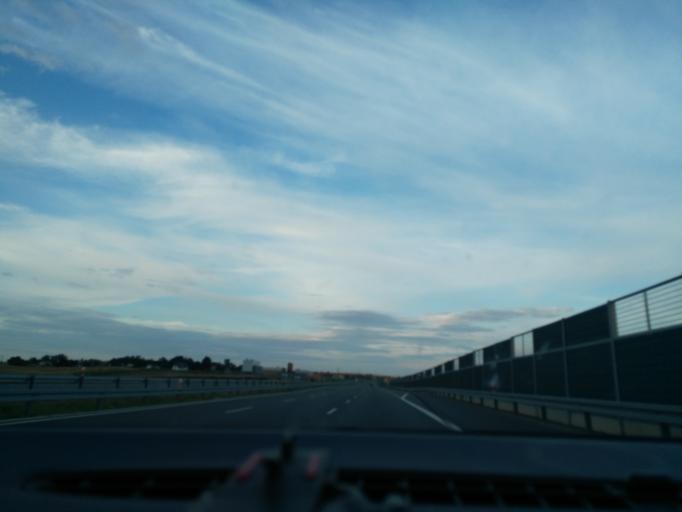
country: PL
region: Lublin Voivodeship
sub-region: Powiat lubelski
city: Lublin
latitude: 51.2986
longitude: 22.5495
